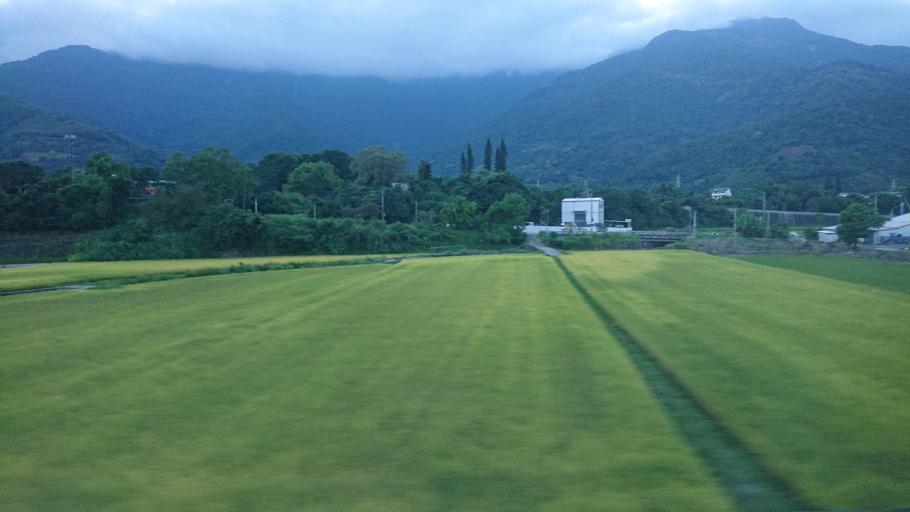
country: TW
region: Taiwan
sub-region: Taitung
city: Taitung
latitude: 23.0404
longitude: 121.1628
